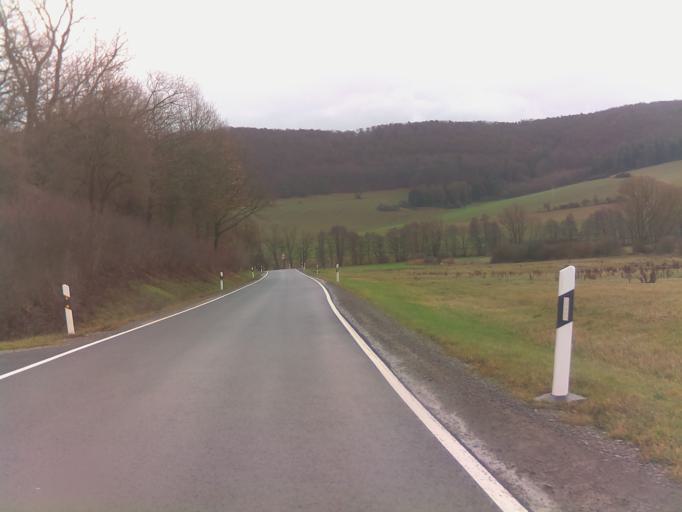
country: DE
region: Thuringia
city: Stepfershausen
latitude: 50.5678
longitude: 10.3126
